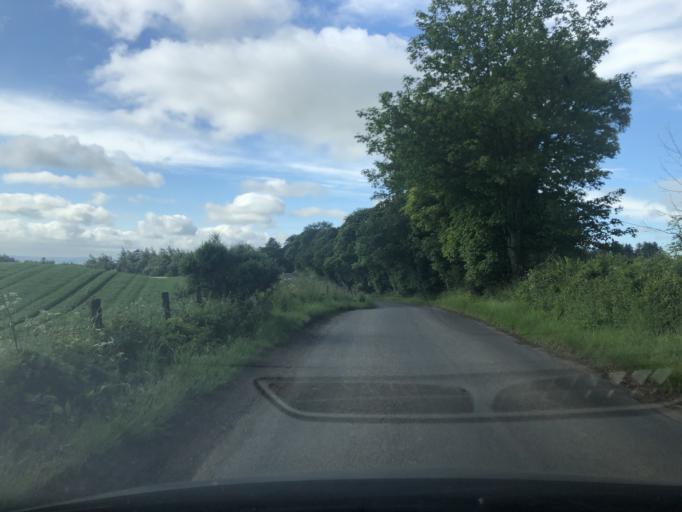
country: GB
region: Scotland
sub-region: Angus
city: Kirriemuir
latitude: 56.7342
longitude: -3.0044
